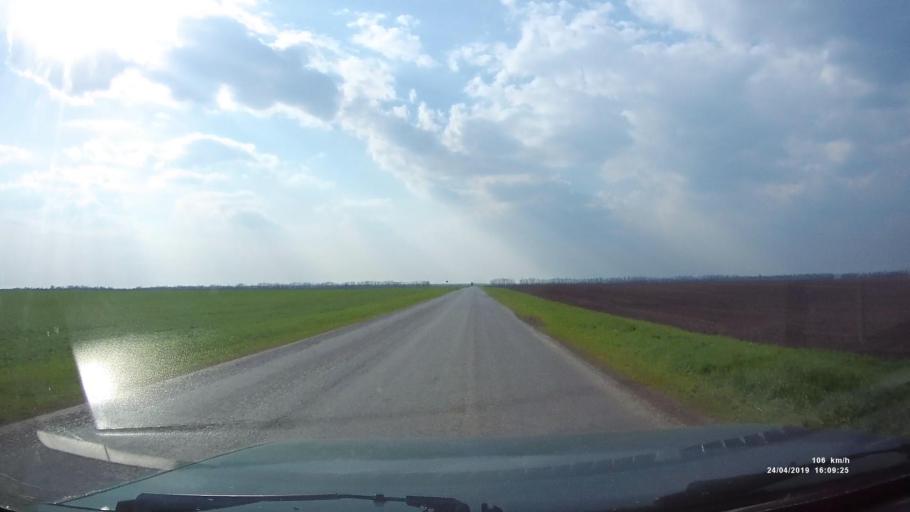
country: RU
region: Rostov
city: Sovetskoye
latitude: 46.7077
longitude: 42.2903
